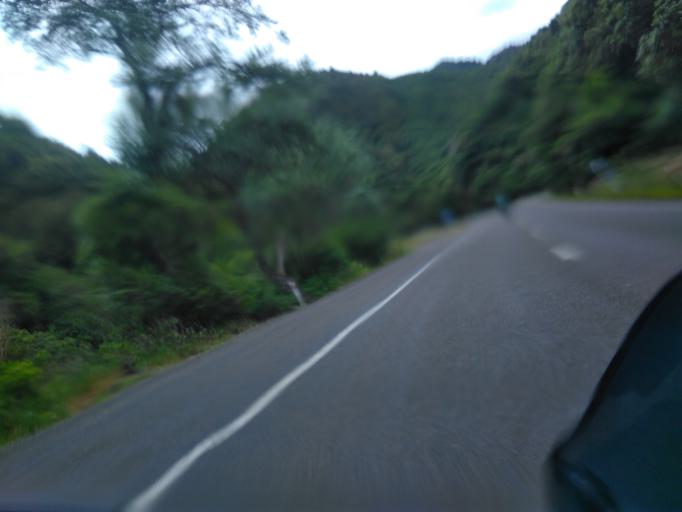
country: NZ
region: Bay of Plenty
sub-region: Opotiki District
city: Opotiki
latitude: -38.3394
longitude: 177.4248
